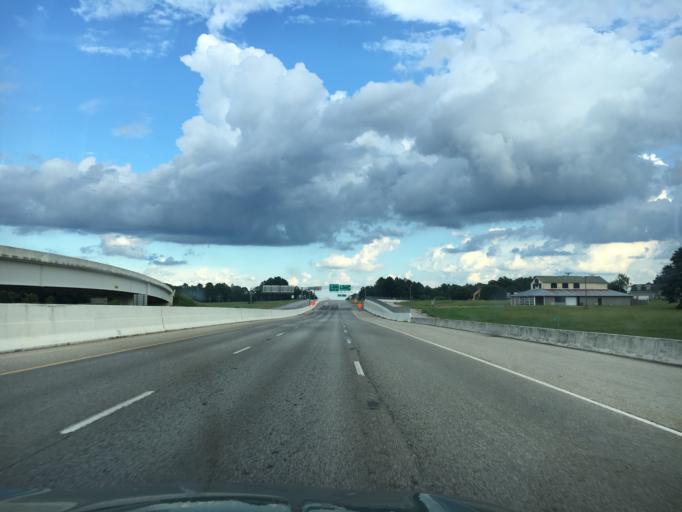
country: US
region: South Carolina
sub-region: Spartanburg County
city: Valley Falls
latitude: 34.9925
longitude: -81.9700
